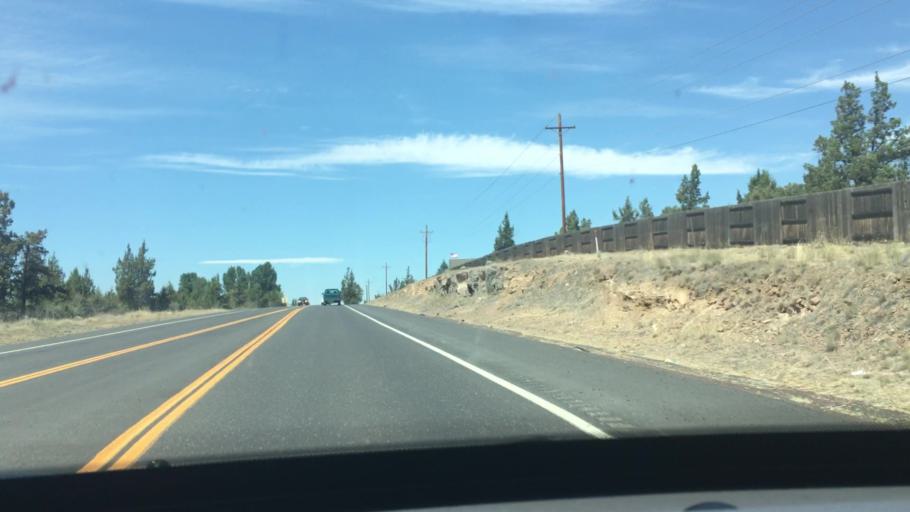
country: US
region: Oregon
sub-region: Deschutes County
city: Terrebonne
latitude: 44.3610
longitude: -121.1785
